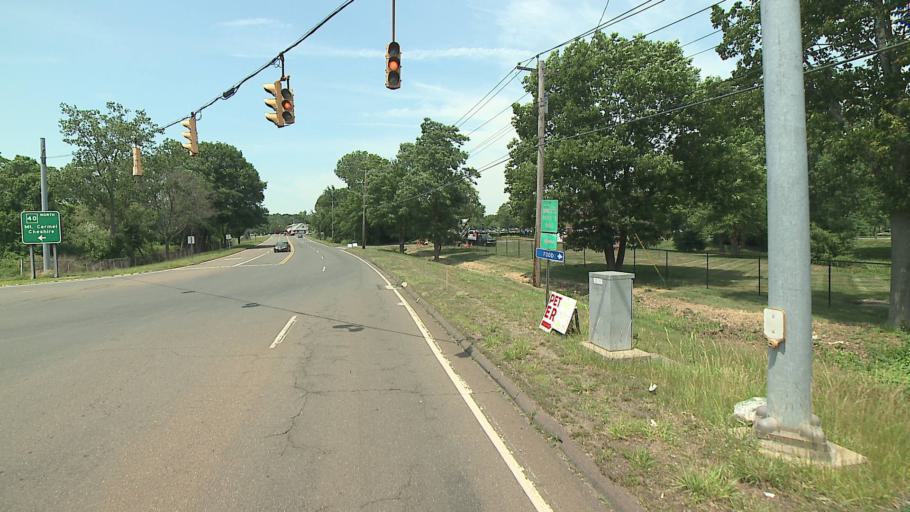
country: US
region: Connecticut
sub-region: New Haven County
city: Hamden
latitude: 41.3802
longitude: -72.8803
